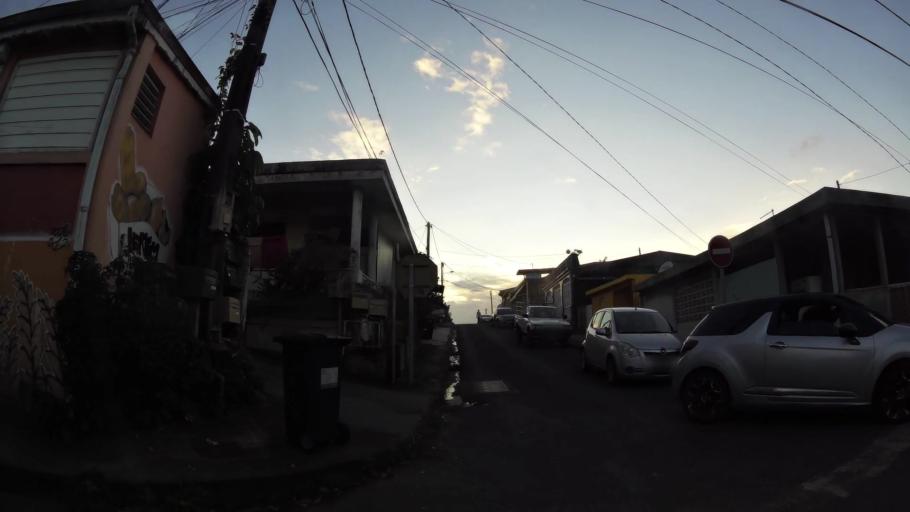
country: GP
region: Guadeloupe
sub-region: Guadeloupe
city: Les Abymes
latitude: 16.2667
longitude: -61.5020
